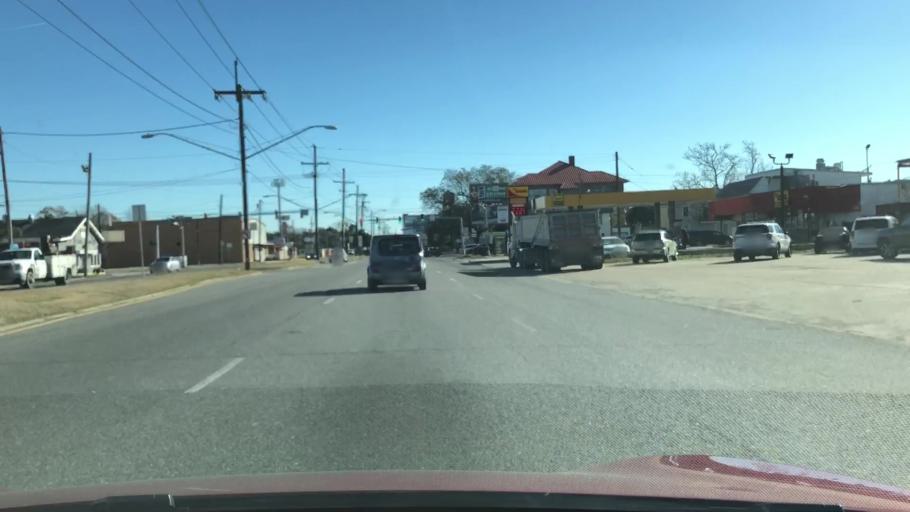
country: US
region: Louisiana
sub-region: Jefferson Parish
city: Jefferson
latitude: 29.9631
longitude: -90.1622
